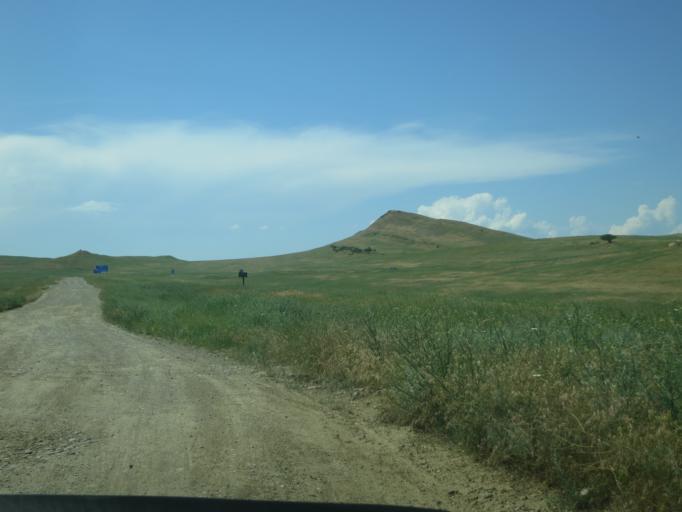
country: AZ
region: Agstafa
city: Saloglu
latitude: 41.4696
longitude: 45.3193
